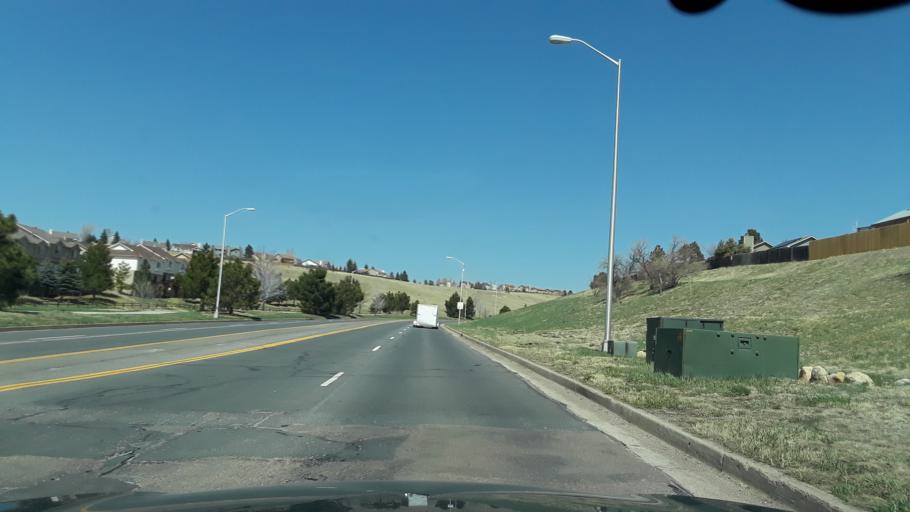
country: US
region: Colorado
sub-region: El Paso County
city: Black Forest
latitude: 38.9458
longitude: -104.7424
